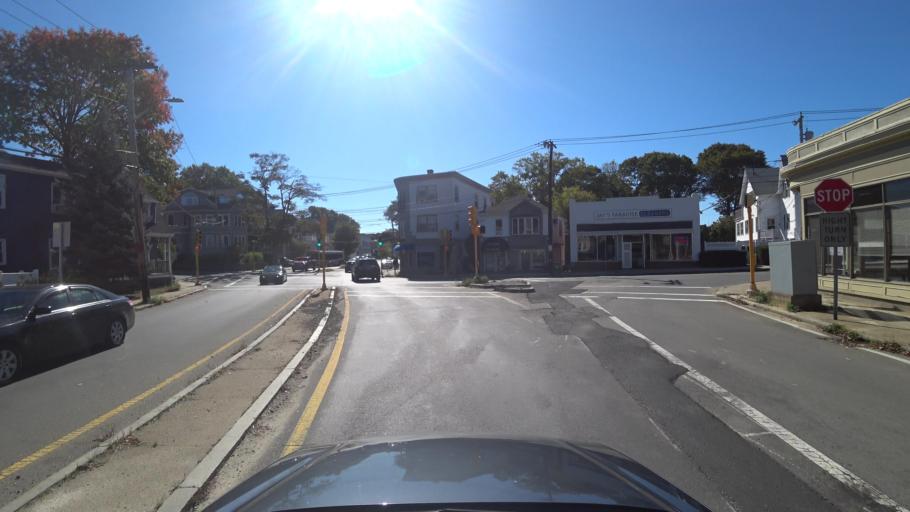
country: US
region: Massachusetts
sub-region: Essex County
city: Swampscott
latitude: 42.4711
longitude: -70.9212
